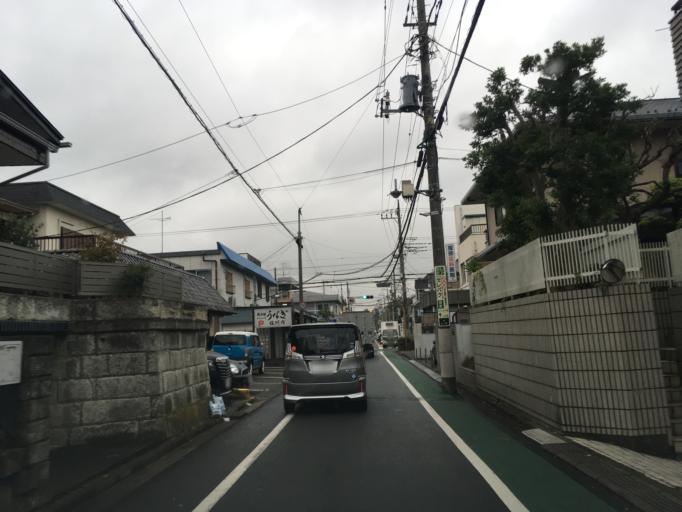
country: JP
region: Tokyo
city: Kokubunji
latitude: 35.6910
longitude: 139.4413
